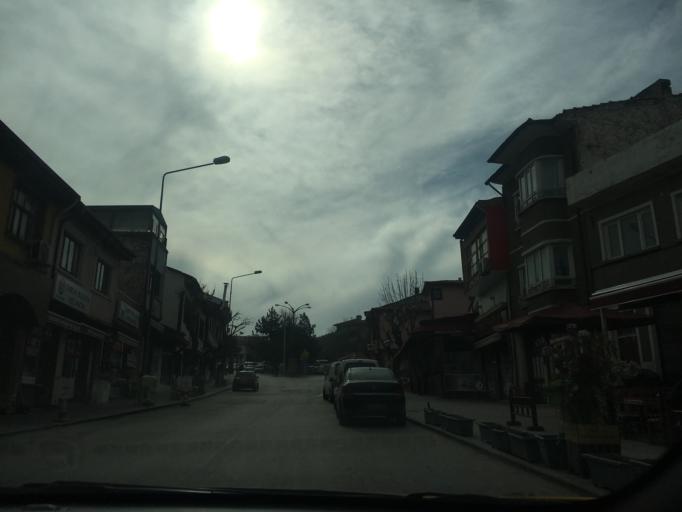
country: TR
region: Eskisehir
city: Eskisehir
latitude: 39.7642
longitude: 30.5242
